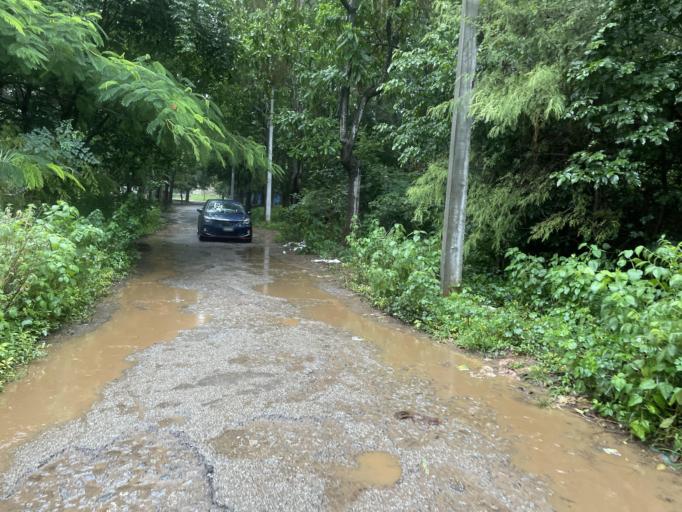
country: IN
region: Karnataka
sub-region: Bangalore Urban
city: Bangalore
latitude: 12.9428
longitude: 77.5025
